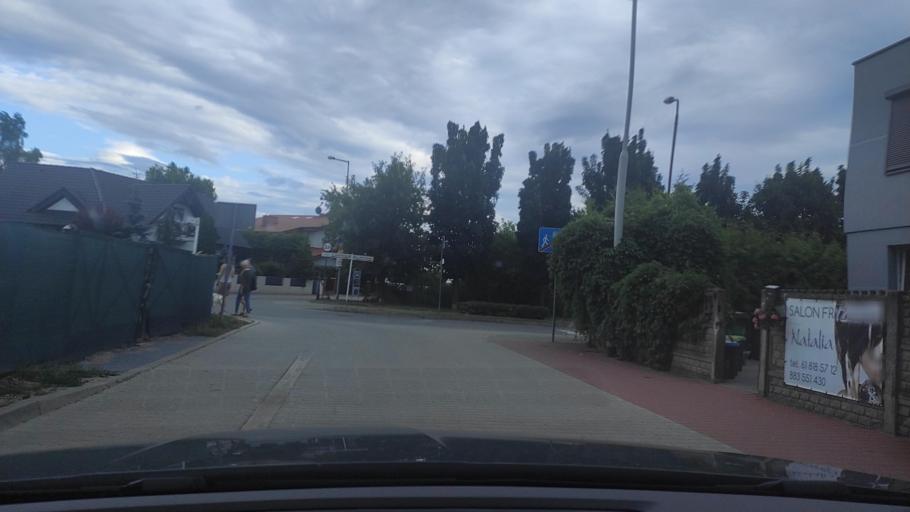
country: PL
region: Greater Poland Voivodeship
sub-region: Powiat poznanski
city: Swarzedz
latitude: 52.3957
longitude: 17.0617
